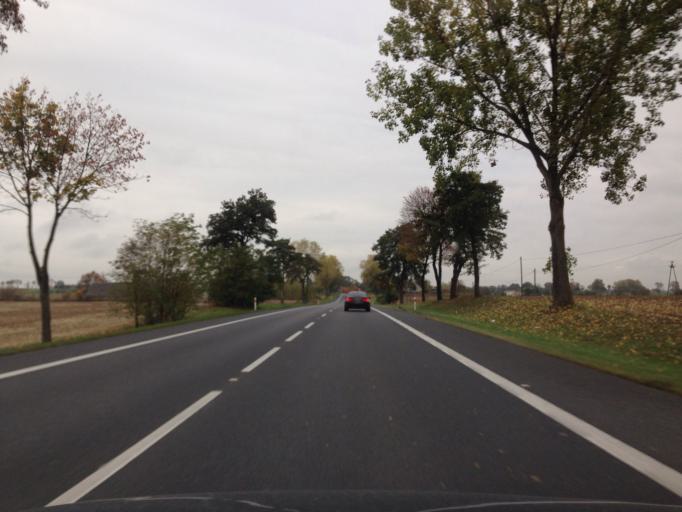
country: PL
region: Kujawsko-Pomorskie
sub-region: Powiat swiecki
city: Pruszcz
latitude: 53.3157
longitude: 18.2714
